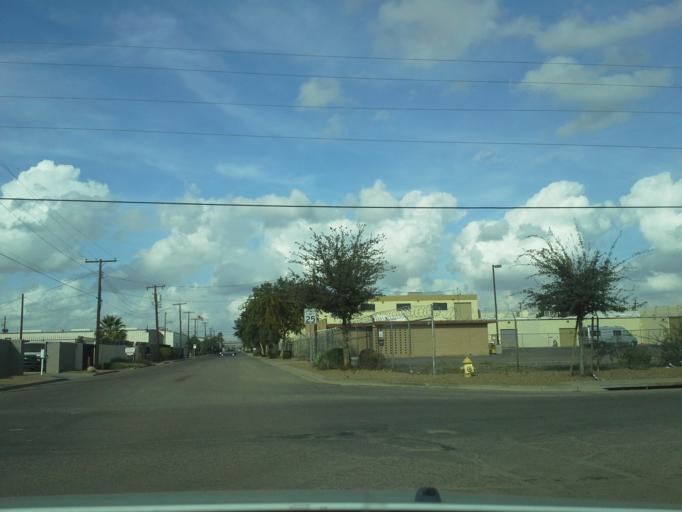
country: US
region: Arizona
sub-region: Maricopa County
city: Phoenix
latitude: 33.4242
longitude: -112.0867
